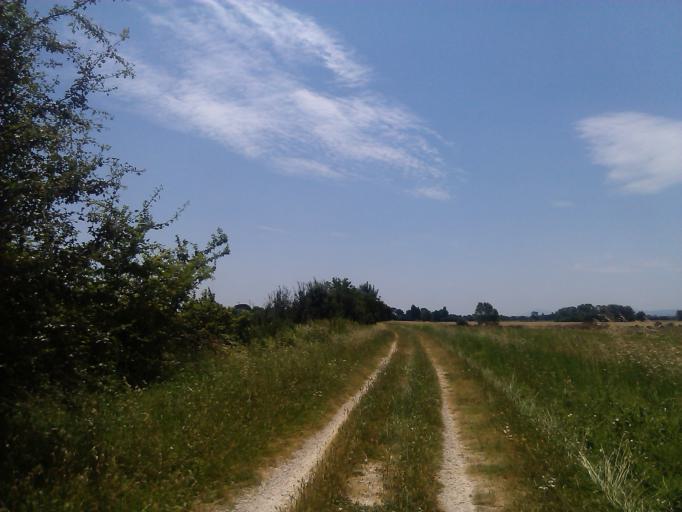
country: IT
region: Tuscany
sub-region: Province of Arezzo
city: Cesa
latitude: 43.3268
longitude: 11.8326
